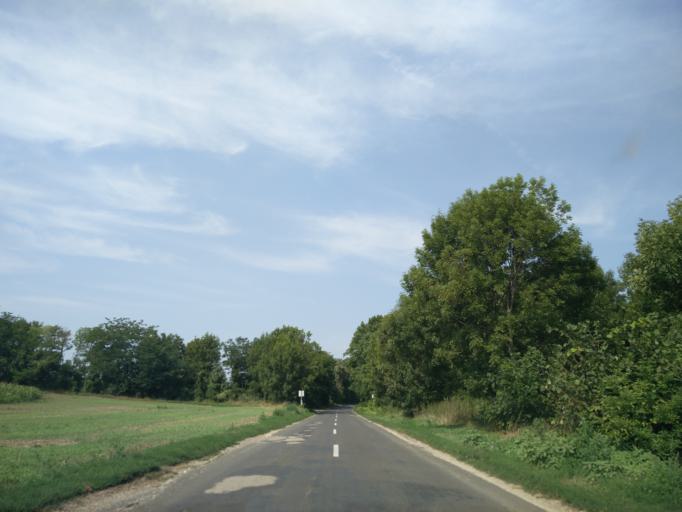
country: HU
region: Fejer
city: Bicske
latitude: 47.4306
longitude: 18.6734
